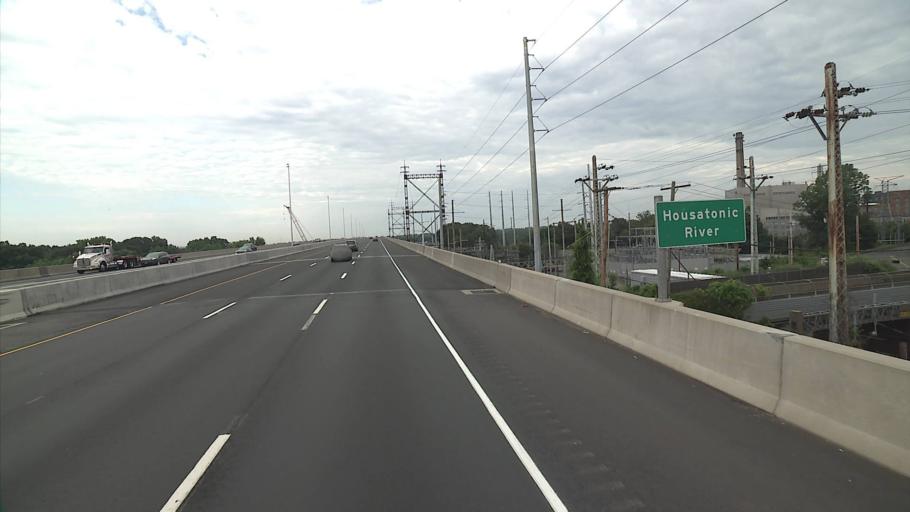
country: US
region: Connecticut
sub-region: Fairfield County
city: Stratford
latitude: 41.2065
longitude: -73.1039
